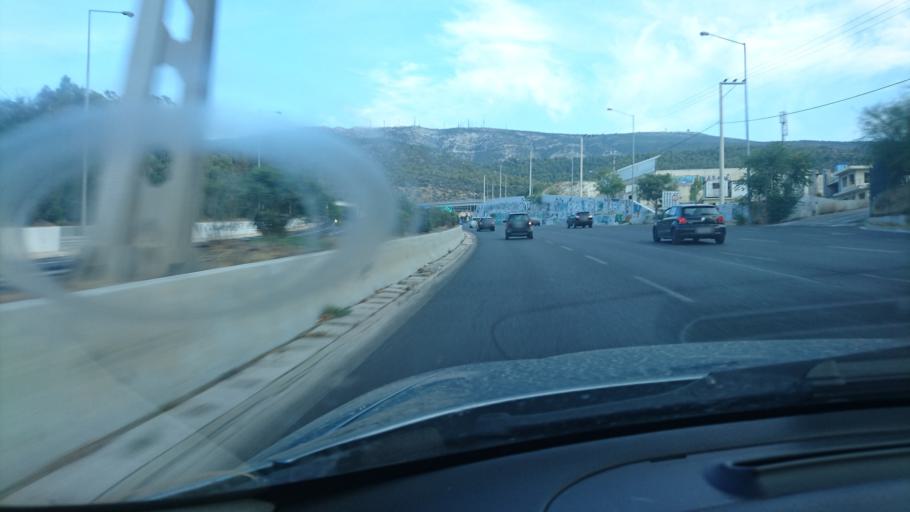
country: GR
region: Attica
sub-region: Nomos Attikis
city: Zografos
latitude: 37.9754
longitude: 23.7902
